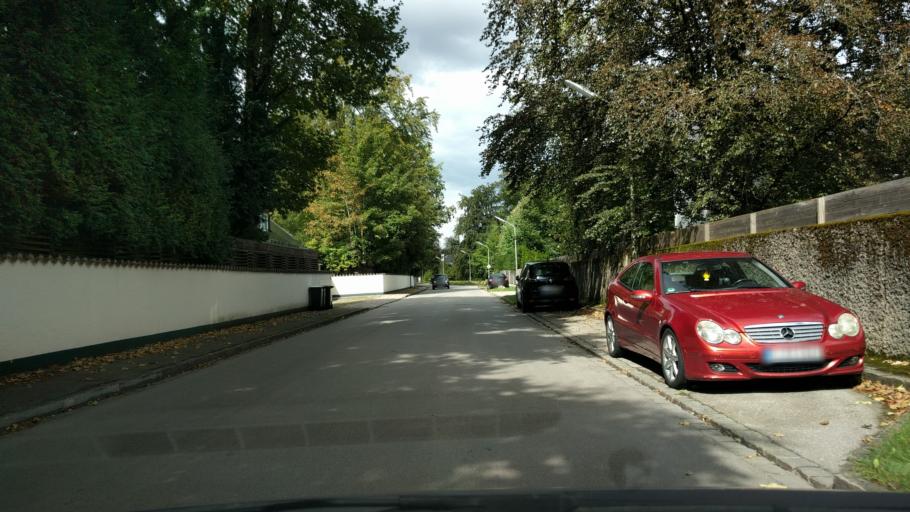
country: DE
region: Bavaria
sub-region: Upper Bavaria
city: Pullach im Isartal
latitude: 48.0591
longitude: 11.5474
